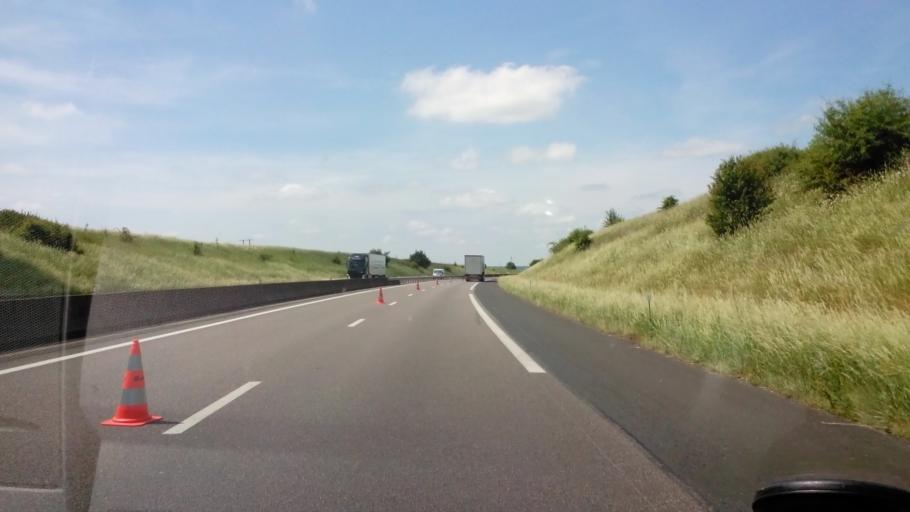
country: FR
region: Lorraine
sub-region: Departement des Vosges
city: Bulgneville
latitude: 48.2295
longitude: 5.8586
